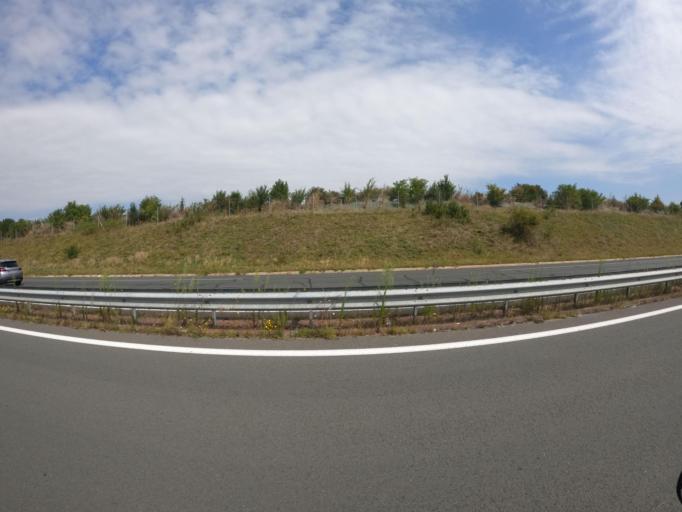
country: FR
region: Poitou-Charentes
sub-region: Departement de la Charente-Maritime
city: Saint-Jean-de-Liversay
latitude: 46.2248
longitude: -0.8627
